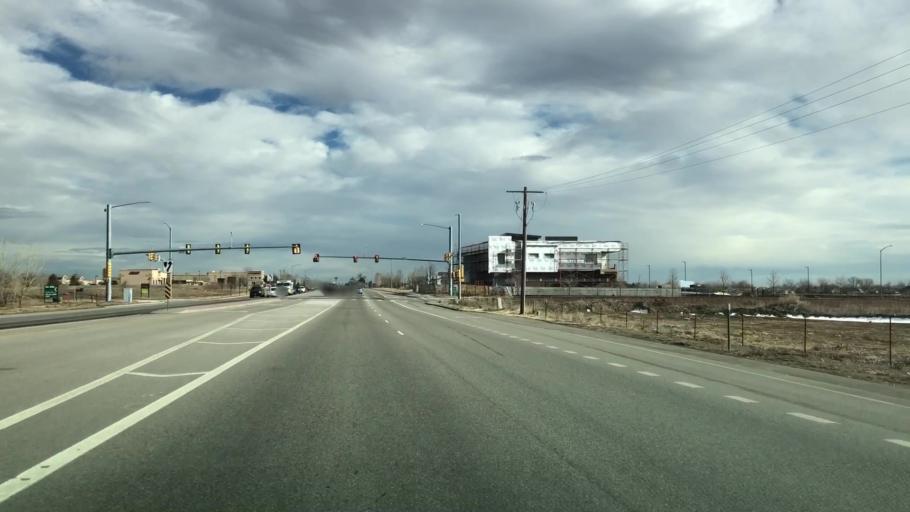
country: US
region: Colorado
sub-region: Weld County
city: Windsor
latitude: 40.4793
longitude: -104.9362
